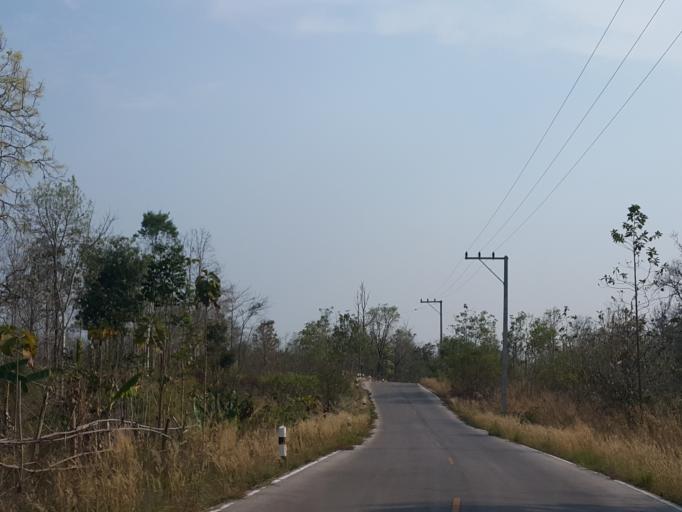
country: TH
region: Lampang
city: Chae Hom
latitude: 18.7350
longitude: 99.5465
